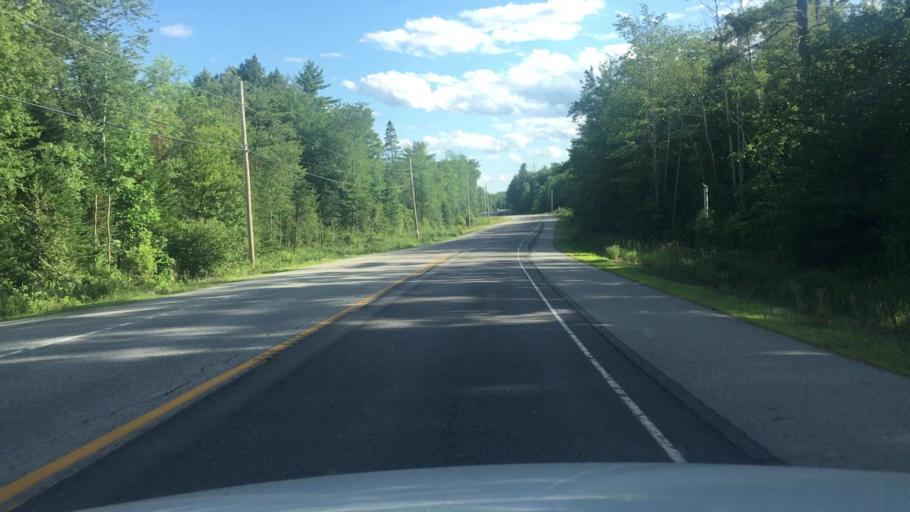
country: US
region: Maine
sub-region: Androscoggin County
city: Livermore
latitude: 44.4051
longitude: -70.2255
